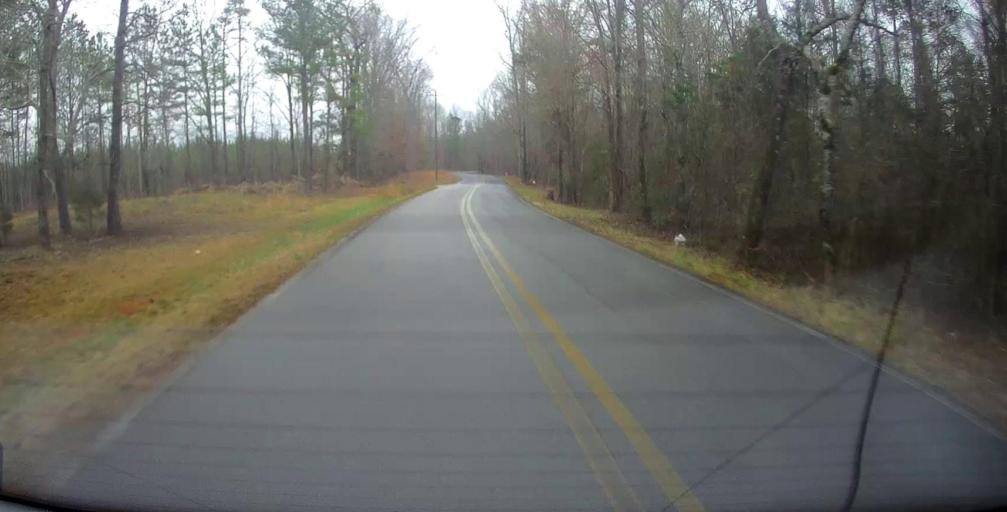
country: US
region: Georgia
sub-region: Monroe County
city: Forsyth
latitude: 33.0868
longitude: -83.8977
